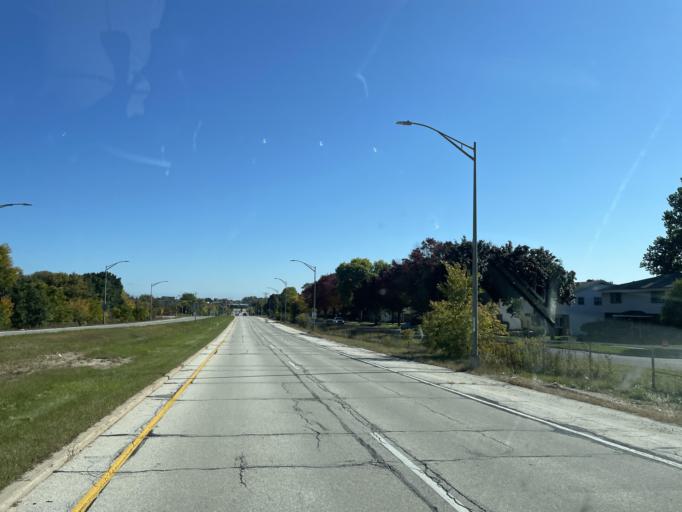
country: US
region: Wisconsin
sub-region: Waukesha County
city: Butler
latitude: 43.1292
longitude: -88.0484
